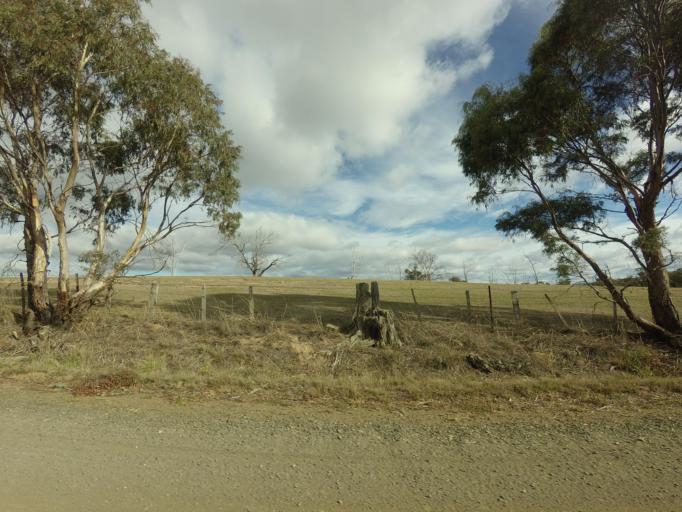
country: AU
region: Tasmania
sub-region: Brighton
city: Bridgewater
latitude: -42.4571
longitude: 147.2505
